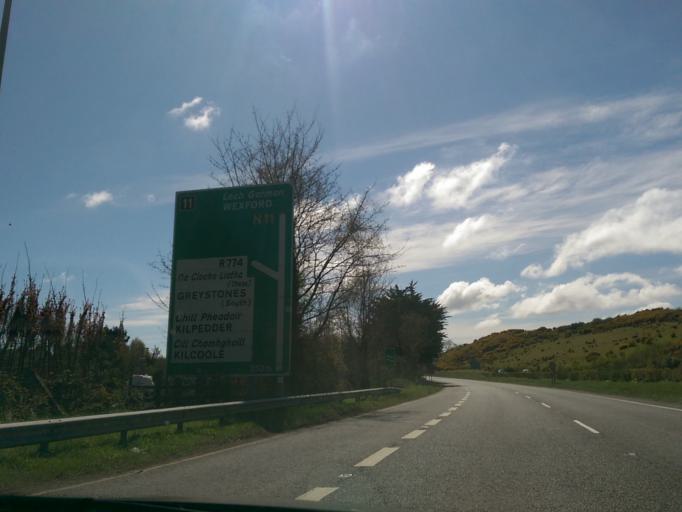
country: IE
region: Leinster
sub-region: Wicklow
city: Kilpedder
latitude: 53.1233
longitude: -6.1048
